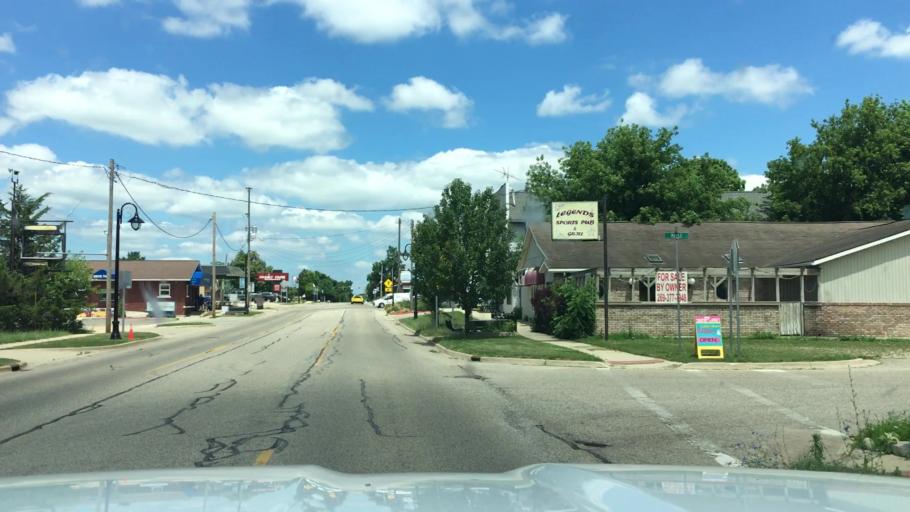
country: US
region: Michigan
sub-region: Barry County
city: Stony Point
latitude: 42.4989
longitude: -85.4080
